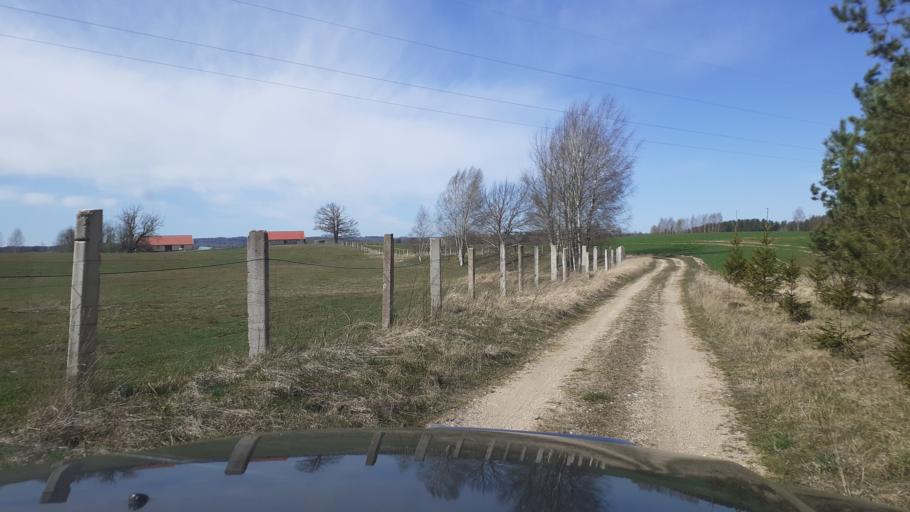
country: LV
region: Skrunda
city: Skrunda
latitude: 56.8300
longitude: 22.0139
